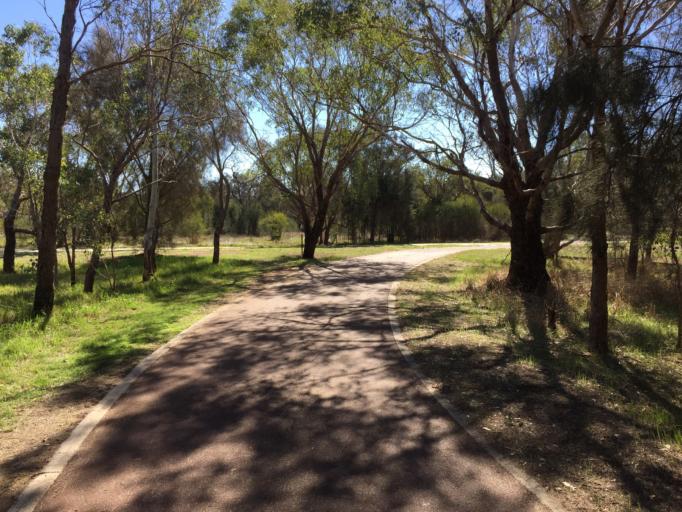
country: AU
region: Western Australia
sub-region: Canning
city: Cannington
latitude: -32.0222
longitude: 115.9340
